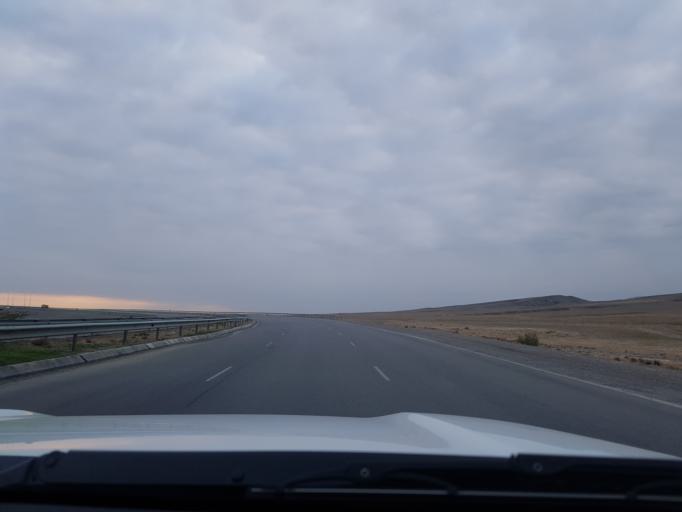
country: IR
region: Razavi Khorasan
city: Dargaz
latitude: 37.6828
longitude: 59.0726
